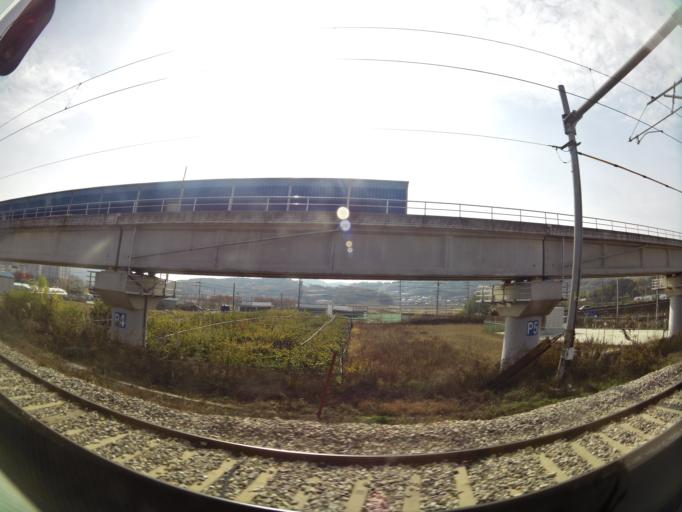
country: KR
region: Daejeon
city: Songgang-dong
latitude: 36.5343
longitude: 127.3563
